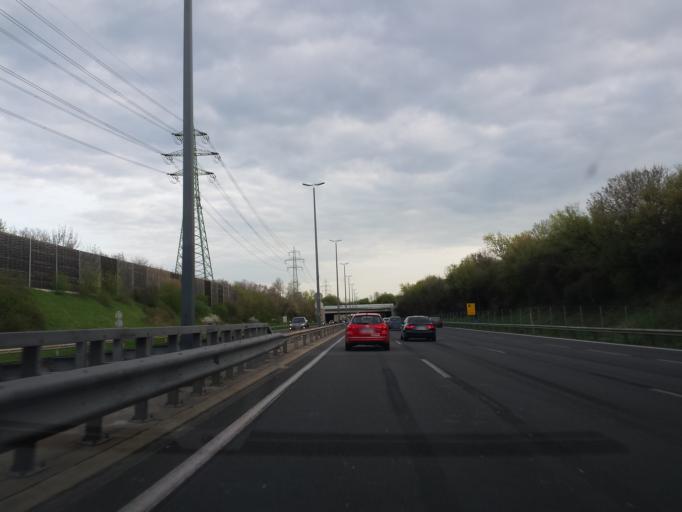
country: AT
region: Lower Austria
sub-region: Politischer Bezirk Korneuburg
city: Langenzersdorf
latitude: 48.2677
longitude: 16.3762
